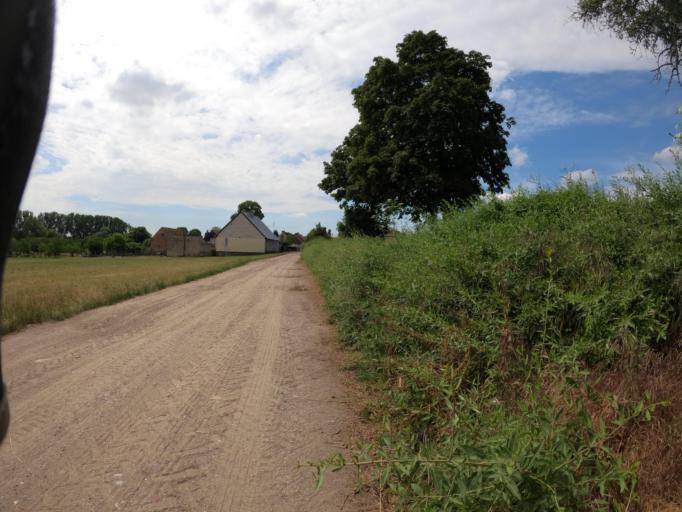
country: DE
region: Brandenburg
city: Letschin
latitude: 52.7337
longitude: 14.3885
